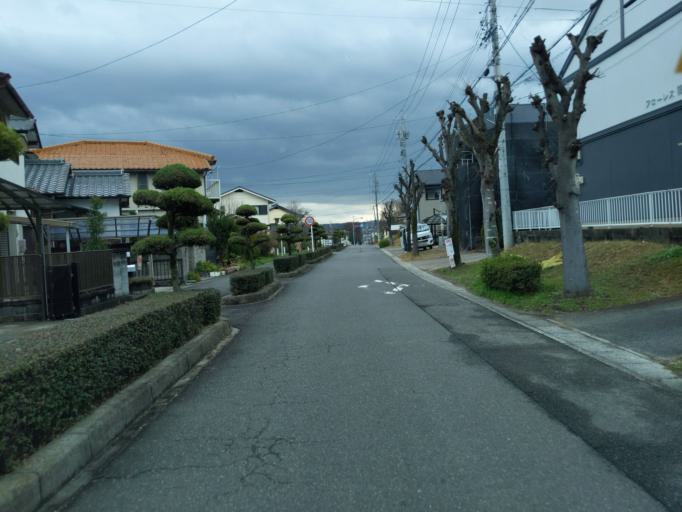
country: JP
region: Aichi
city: Kasugai
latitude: 35.2578
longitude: 136.9880
